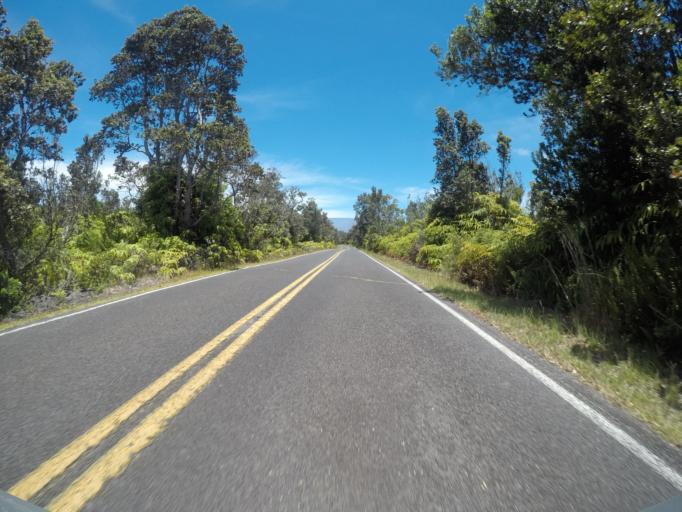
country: US
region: Hawaii
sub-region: Hawaii County
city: Volcano
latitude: 19.3660
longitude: -155.2191
